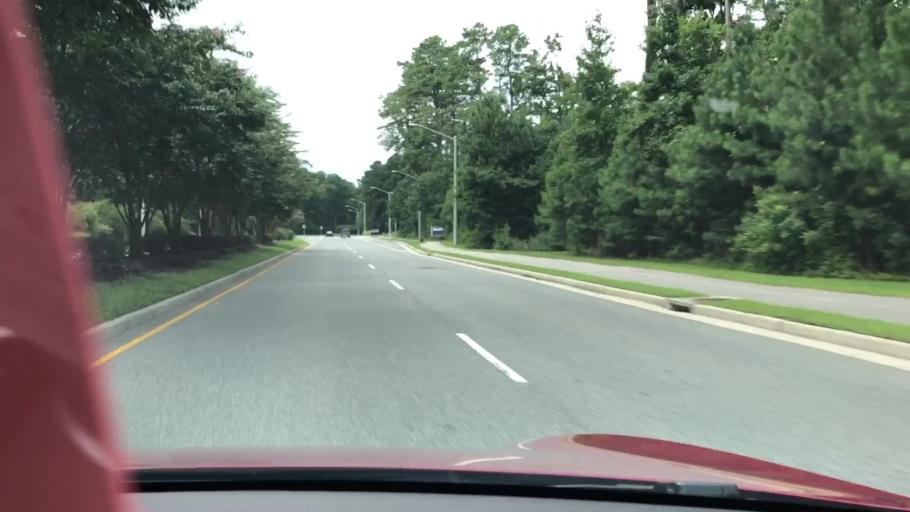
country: US
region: Virginia
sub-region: City of Virginia Beach
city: Virginia Beach
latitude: 36.8144
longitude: -75.9963
